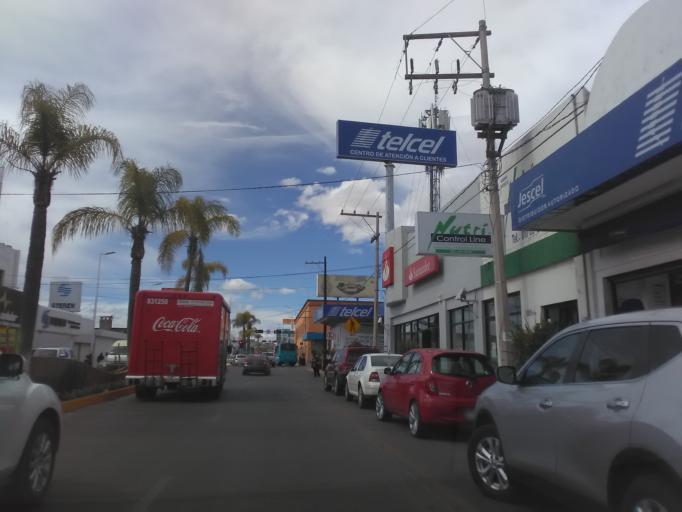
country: MX
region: Durango
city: Victoria de Durango
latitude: 24.0283
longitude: -104.6498
